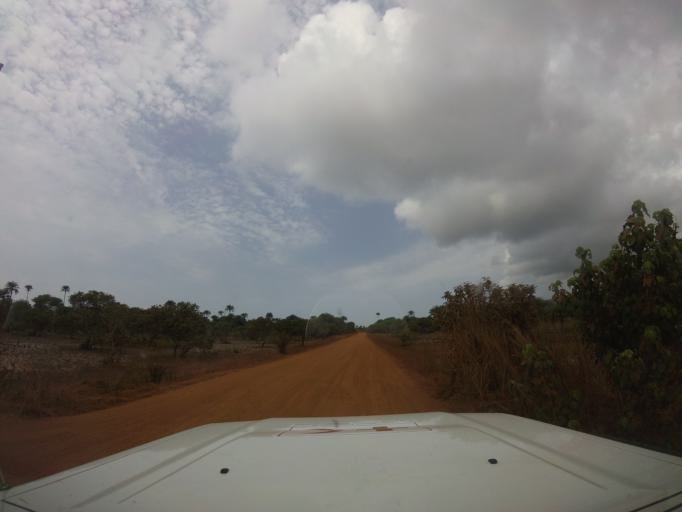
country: LR
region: Grand Cape Mount
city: Robertsport
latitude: 6.7048
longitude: -11.3038
